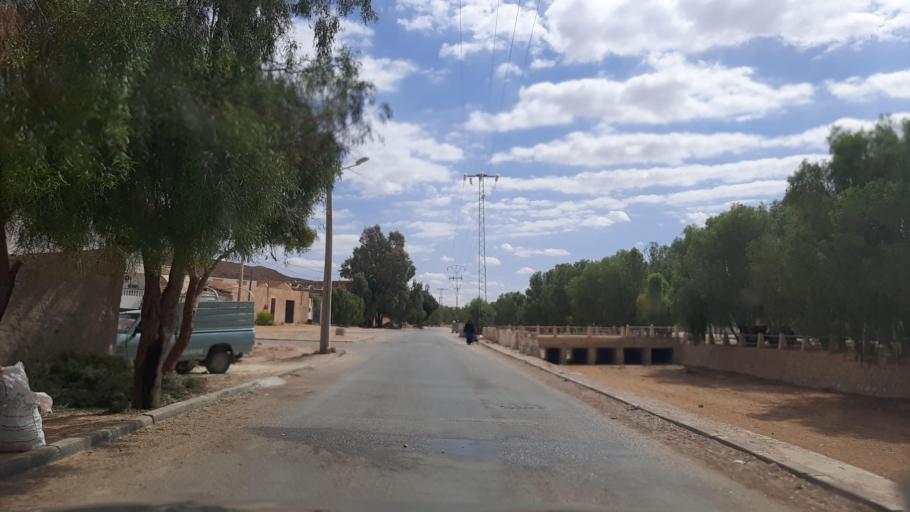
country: TN
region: Tataouine
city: Tataouine
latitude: 32.9262
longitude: 10.4589
